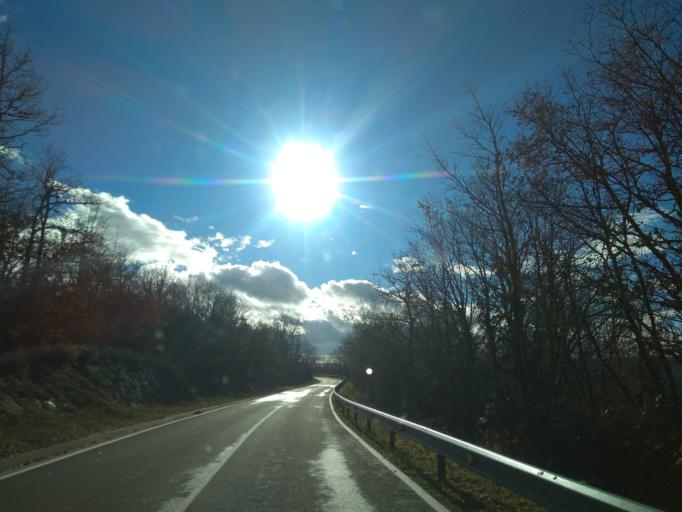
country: ES
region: Cantabria
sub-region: Provincia de Cantabria
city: San Martin de Elines
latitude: 42.9100
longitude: -3.8679
